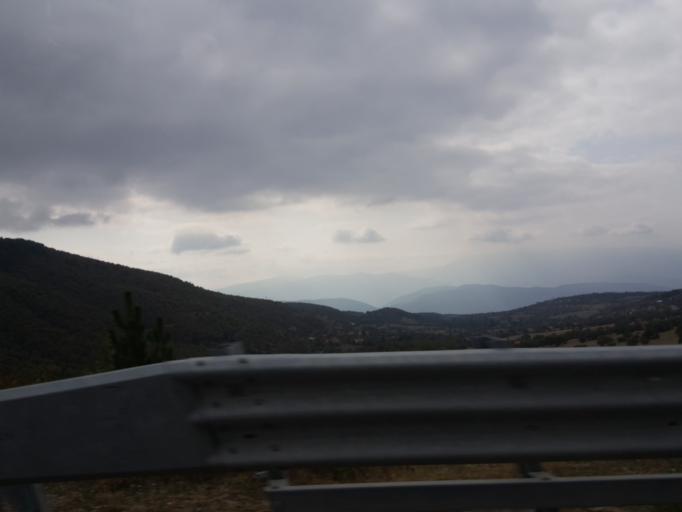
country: TR
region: Corum
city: Kargi
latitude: 41.1779
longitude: 34.5512
